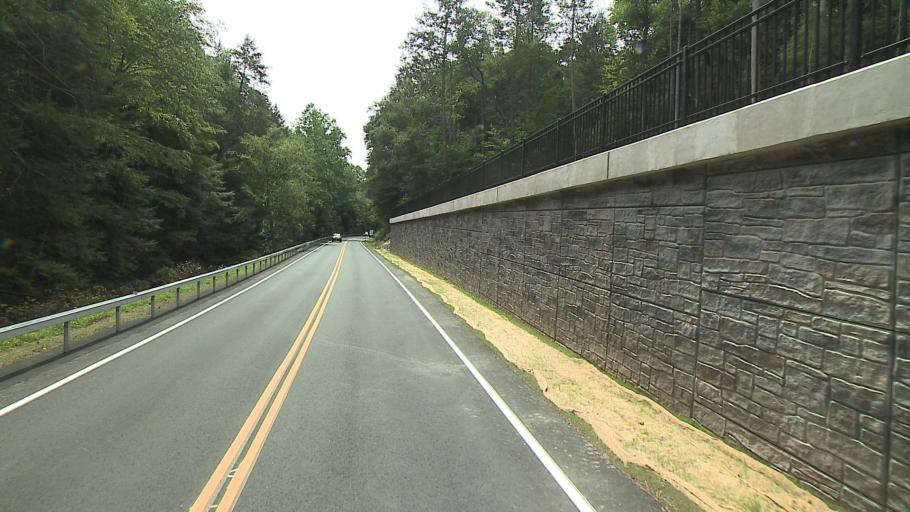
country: US
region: Connecticut
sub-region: Fairfield County
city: Newtown
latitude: 41.4882
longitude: -73.3515
